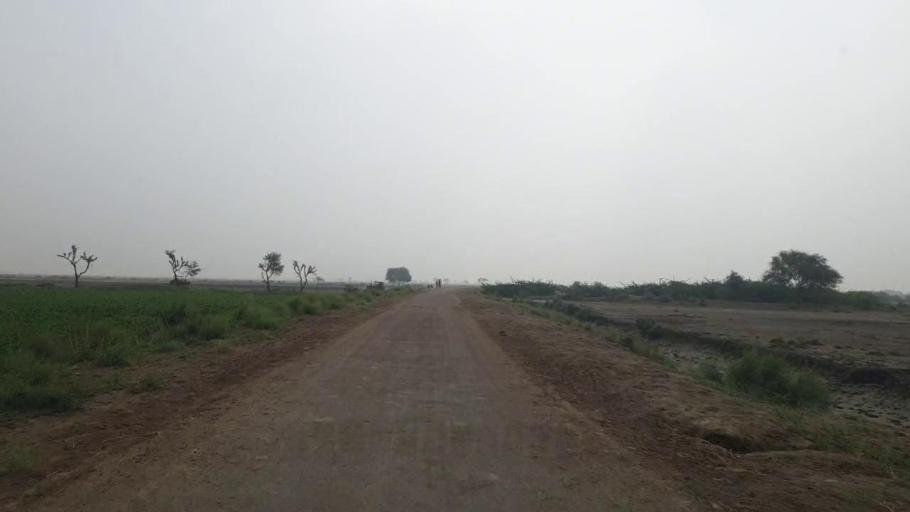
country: PK
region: Sindh
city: Badin
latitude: 24.5736
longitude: 68.6881
